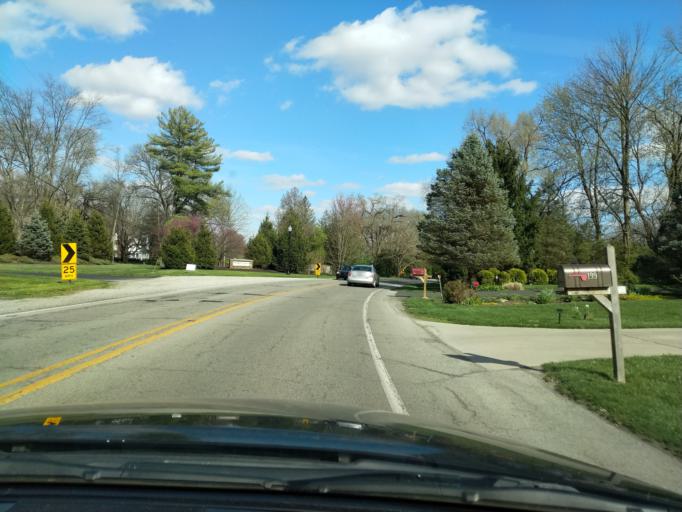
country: US
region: Indiana
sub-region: Marion County
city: Meridian Hills
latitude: 39.8867
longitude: -86.1629
